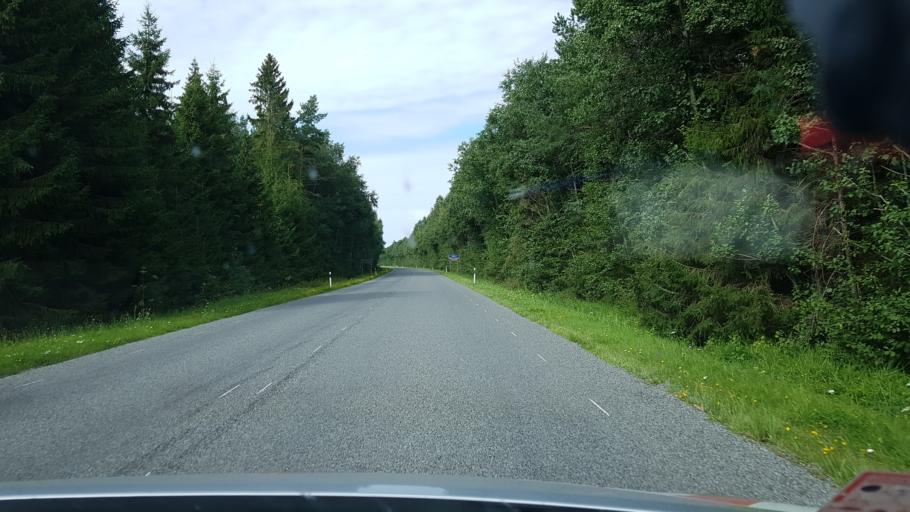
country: EE
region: Paernumaa
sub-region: Tootsi vald
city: Tootsi
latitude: 58.6629
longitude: 24.8165
